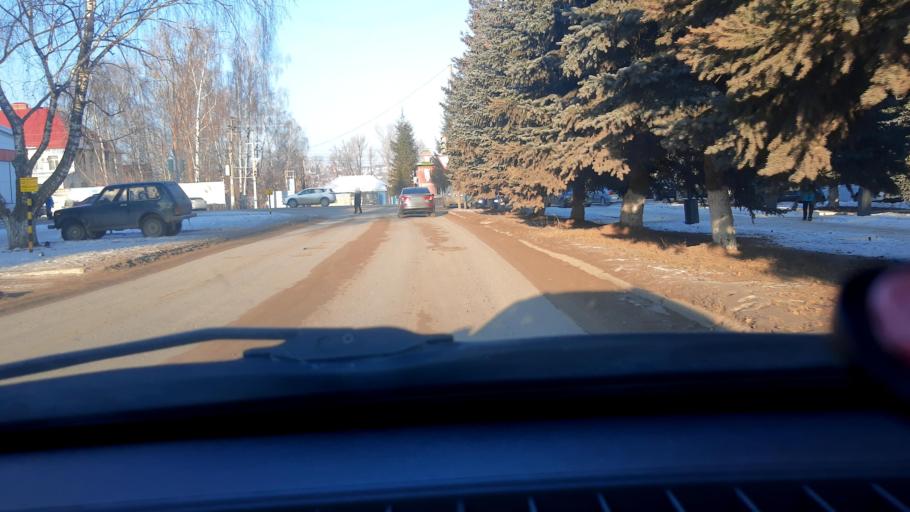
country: RU
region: Bashkortostan
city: Iglino
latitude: 54.8343
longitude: 56.4161
